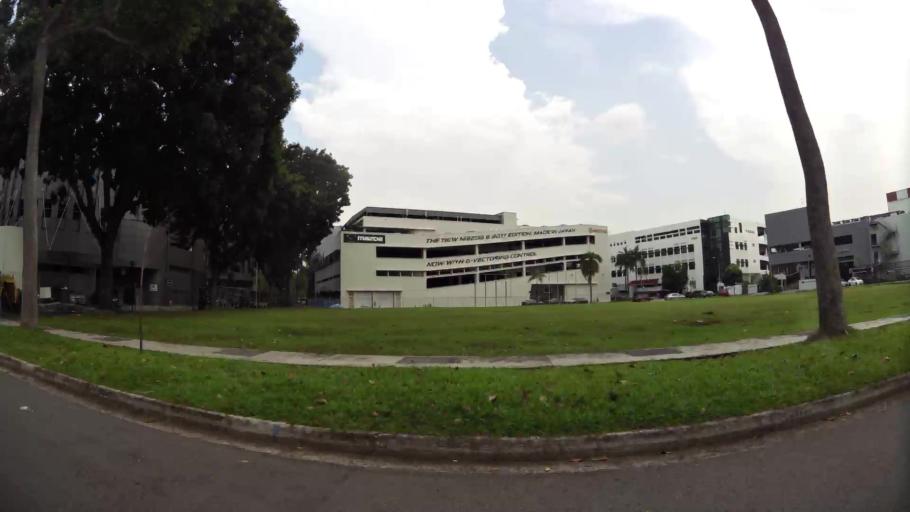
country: SG
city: Singapore
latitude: 1.3347
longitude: 103.8974
